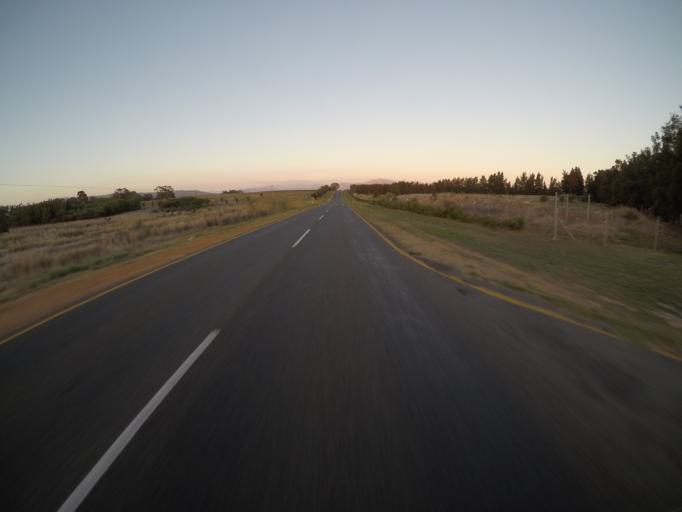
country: ZA
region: Western Cape
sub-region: Cape Winelands District Municipality
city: Paarl
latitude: -33.8060
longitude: 18.8805
